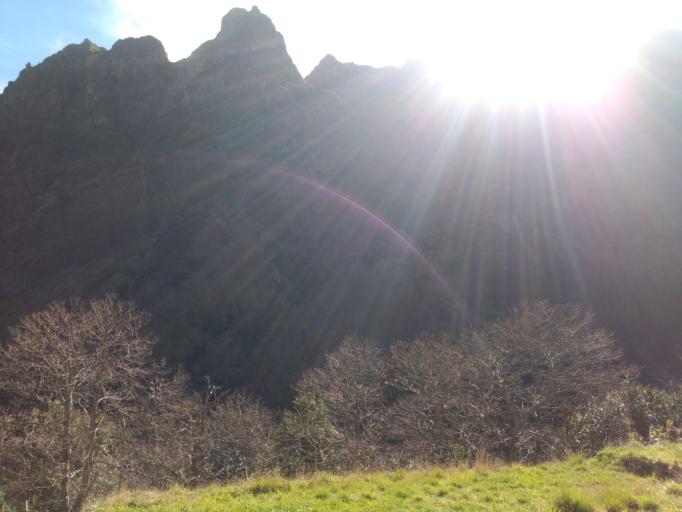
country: PT
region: Madeira
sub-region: Camara de Lobos
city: Curral das Freiras
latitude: 32.7456
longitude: -16.9656
